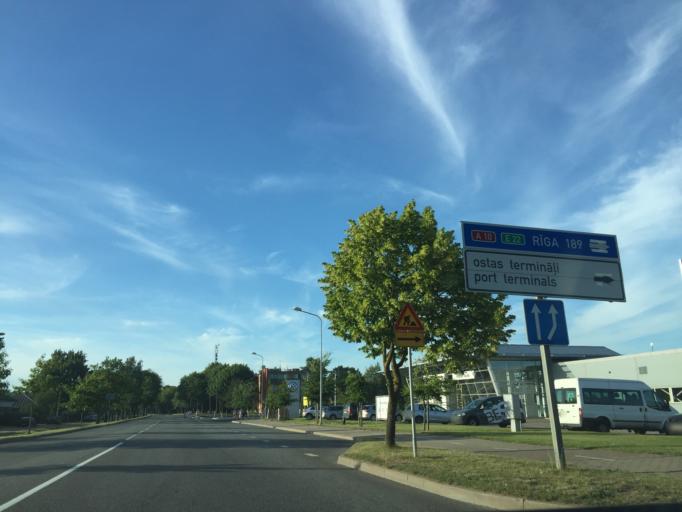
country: LV
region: Ventspils
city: Ventspils
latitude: 57.3787
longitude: 21.5663
